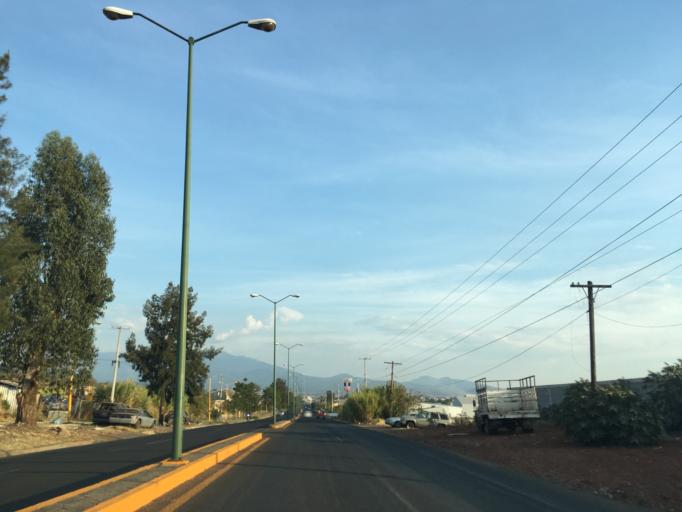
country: MX
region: Michoacan
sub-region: Los Reyes
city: La Higuerita (Colonia San Rafael)
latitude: 19.6110
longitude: -102.4814
